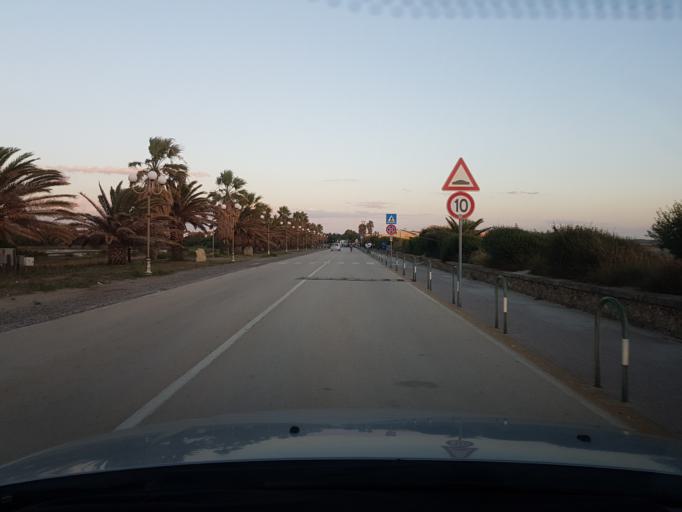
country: IT
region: Sardinia
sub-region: Provincia di Oristano
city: Riola Sardo
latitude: 40.0301
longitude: 8.4059
